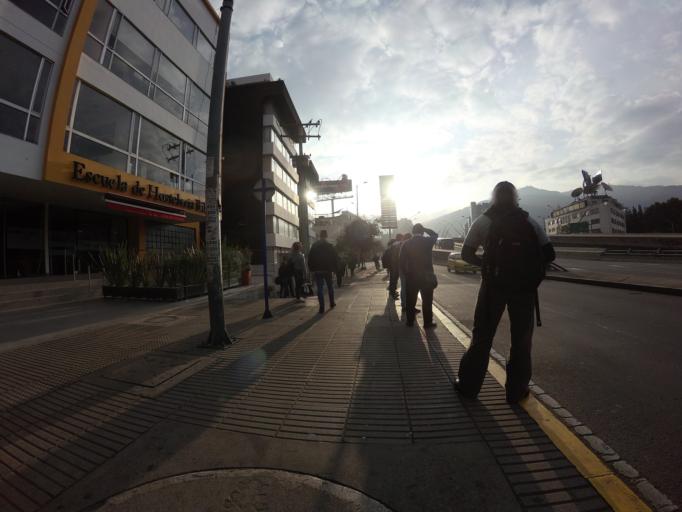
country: CO
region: Bogota D.C.
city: Barrio San Luis
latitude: 4.6858
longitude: -74.0496
